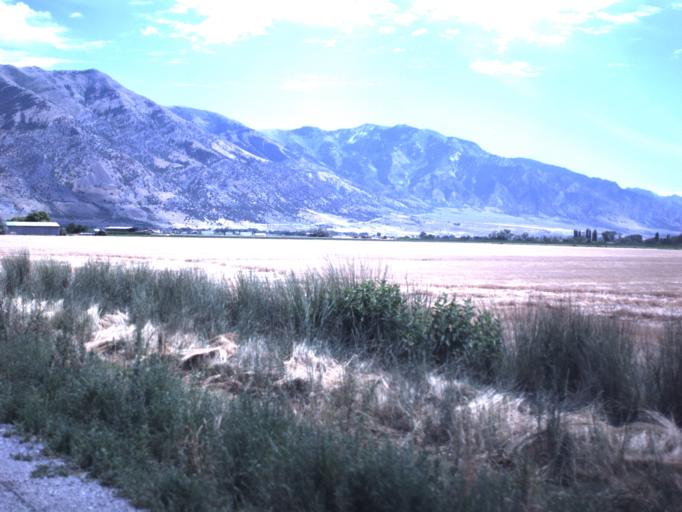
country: US
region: Utah
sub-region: Box Elder County
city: Elwood
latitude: 41.7125
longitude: -112.1321
